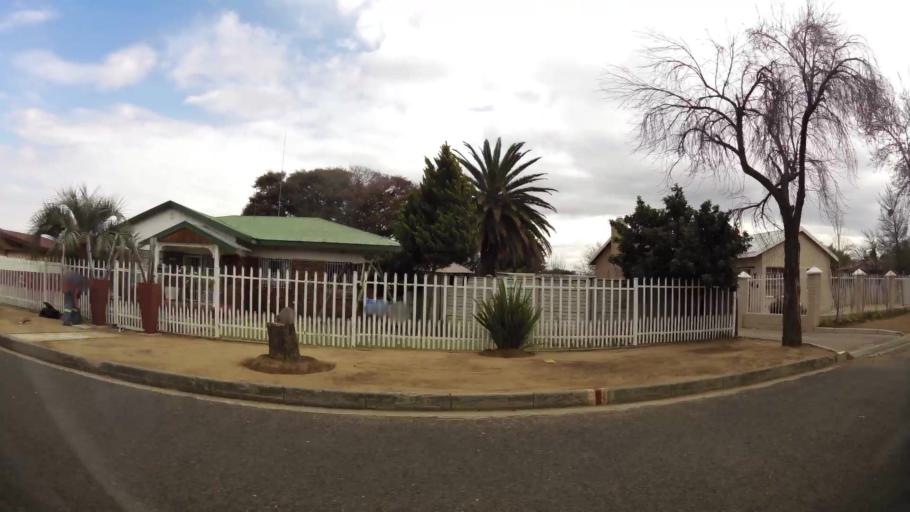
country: ZA
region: Orange Free State
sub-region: Fezile Dabi District Municipality
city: Kroonstad
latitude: -27.6378
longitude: 27.2296
